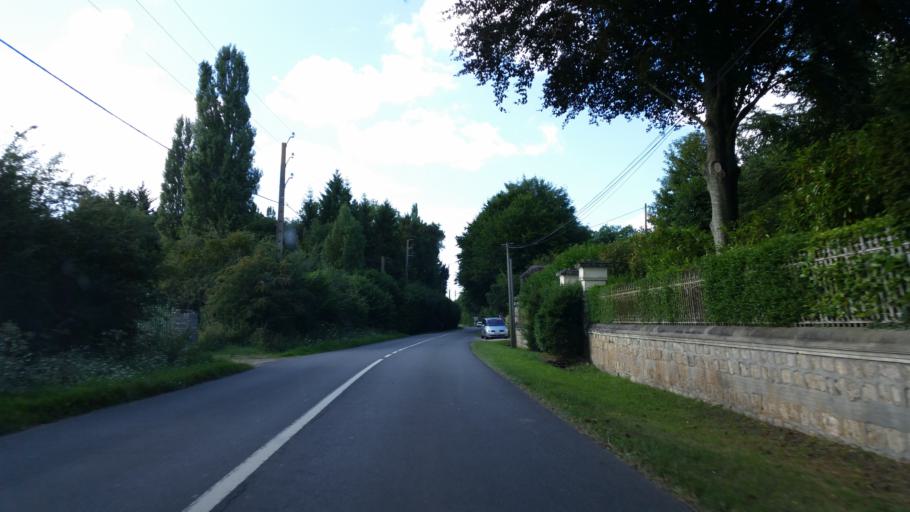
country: FR
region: Lower Normandy
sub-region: Departement du Calvados
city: Touques
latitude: 49.3350
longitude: 0.1114
